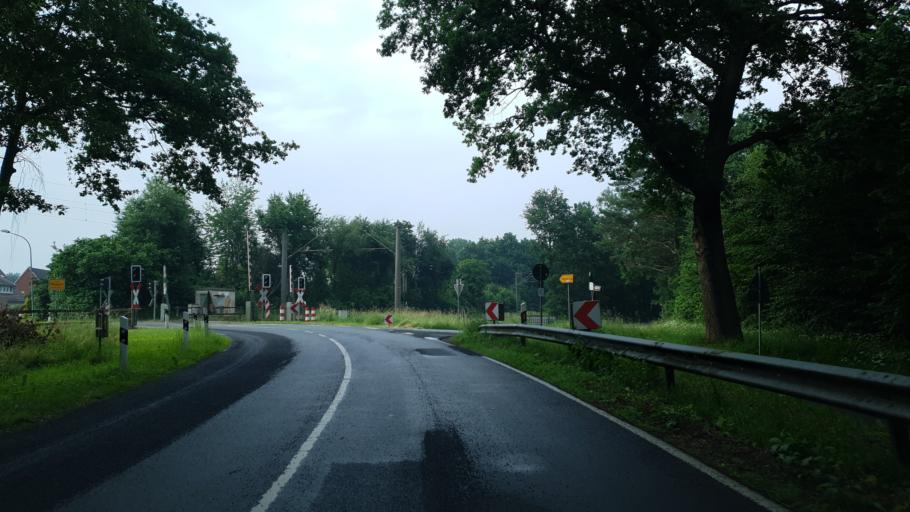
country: DE
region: Lower Saxony
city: Meppen
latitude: 52.6694
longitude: 7.3110
